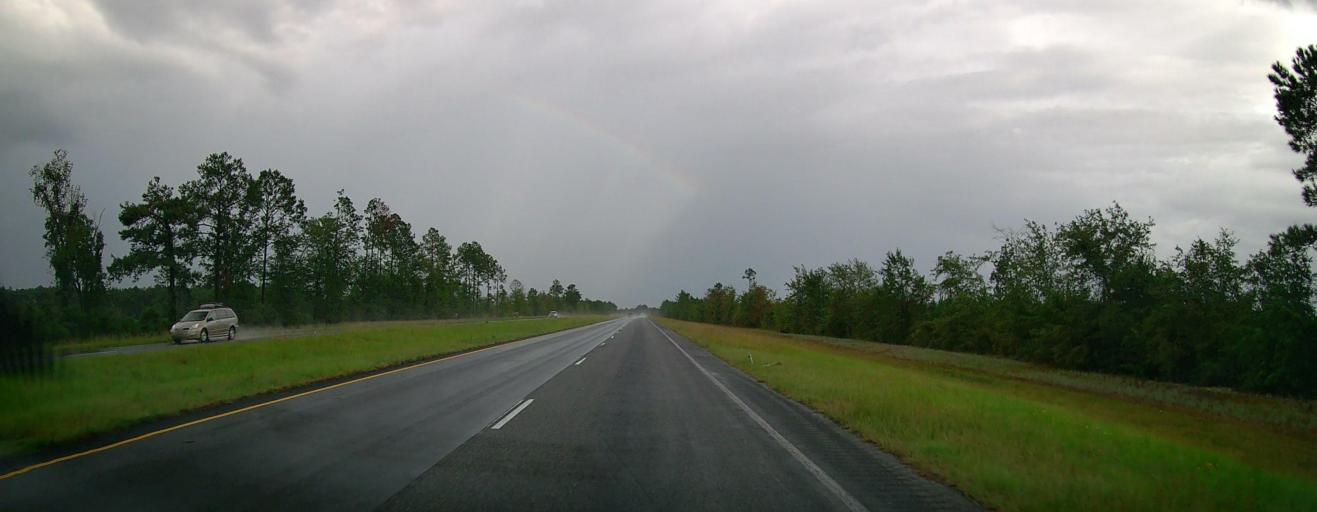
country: US
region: Georgia
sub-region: Ware County
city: Deenwood
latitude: 31.2552
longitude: -82.4609
